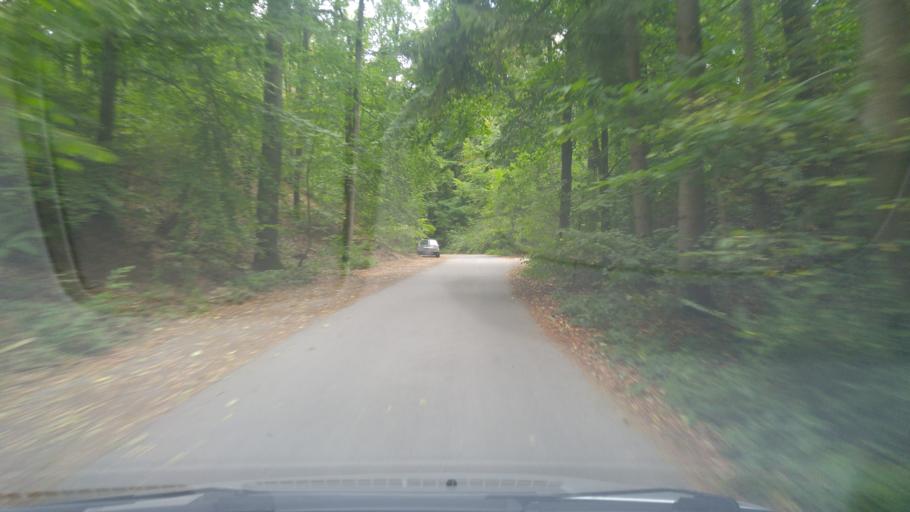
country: DE
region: Baden-Wuerttemberg
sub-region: Regierungsbezirk Stuttgart
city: Renningen
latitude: 48.7750
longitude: 8.9563
